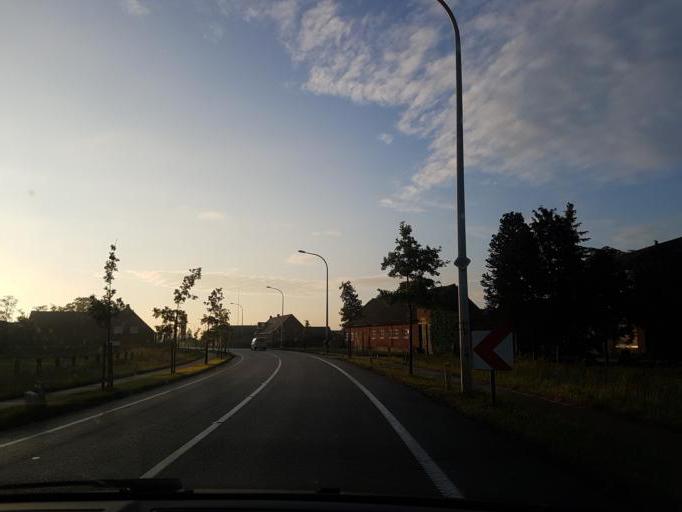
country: BE
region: Flanders
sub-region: Provincie Antwerpen
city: Hoogstraten
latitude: 51.3932
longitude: 4.7109
